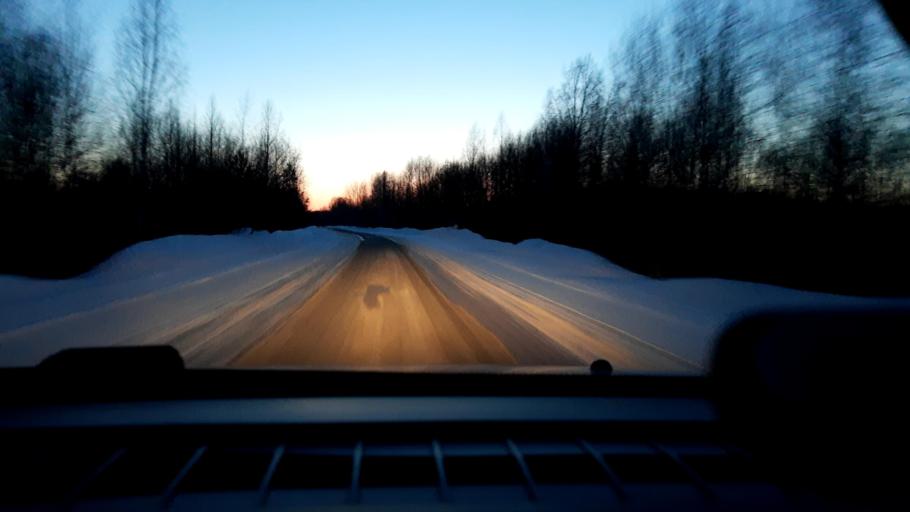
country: RU
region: Nizjnij Novgorod
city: Spasskoye
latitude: 56.1536
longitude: 45.4364
